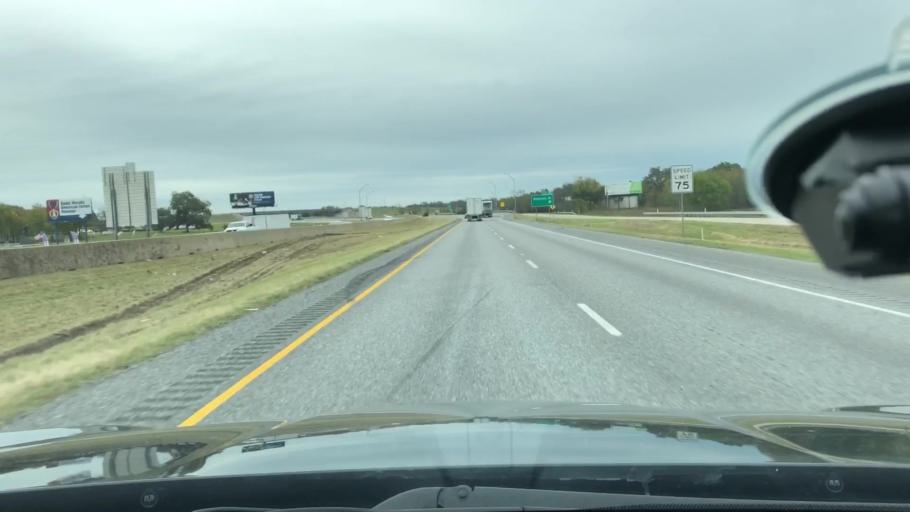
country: US
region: Texas
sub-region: Hunt County
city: Greenville
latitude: 33.1229
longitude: -96.0901
